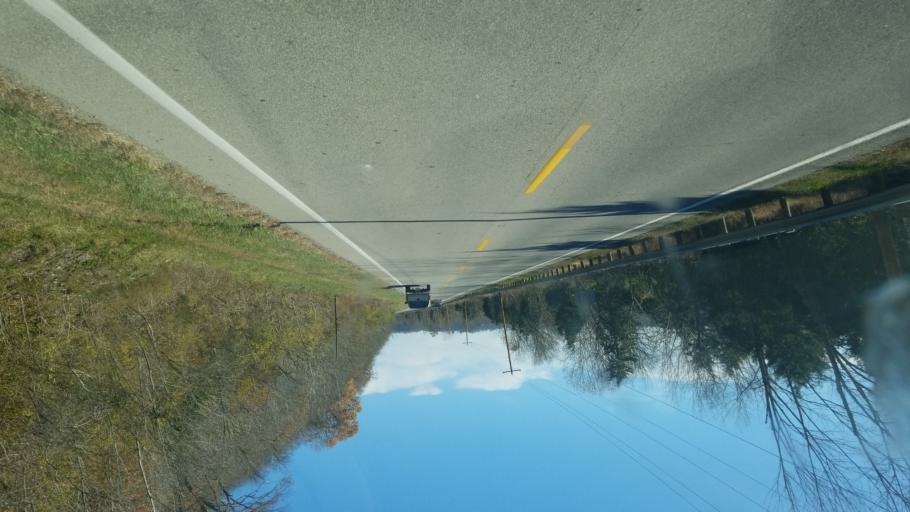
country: US
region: Kentucky
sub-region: Mason County
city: Maysville
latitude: 38.6492
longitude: -83.7363
